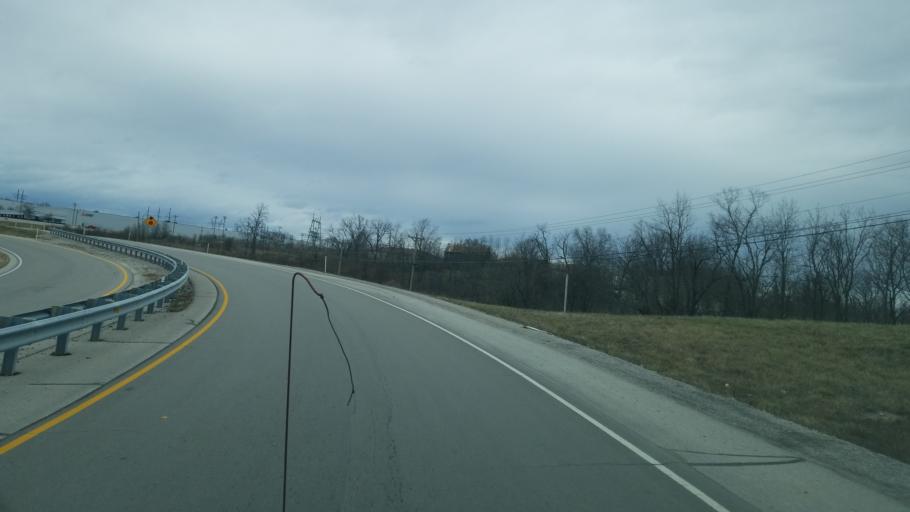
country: US
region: Ohio
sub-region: Brown County
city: Aberdeen
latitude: 38.6440
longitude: -83.8286
